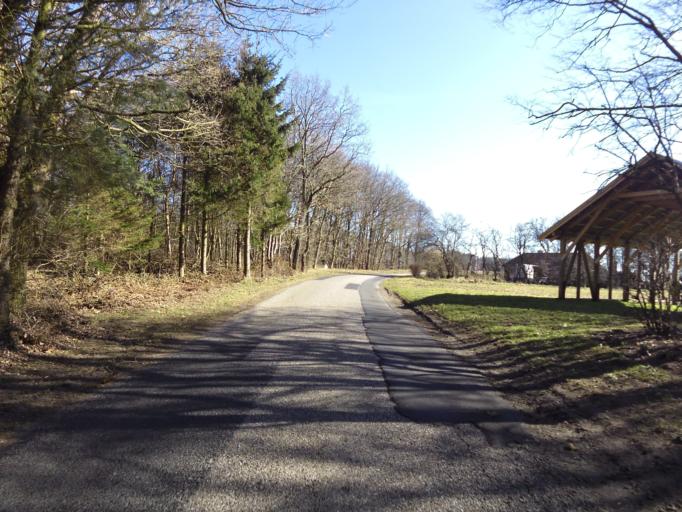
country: DK
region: South Denmark
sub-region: Tonder Kommune
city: Toftlund
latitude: 55.2293
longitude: 9.1382
